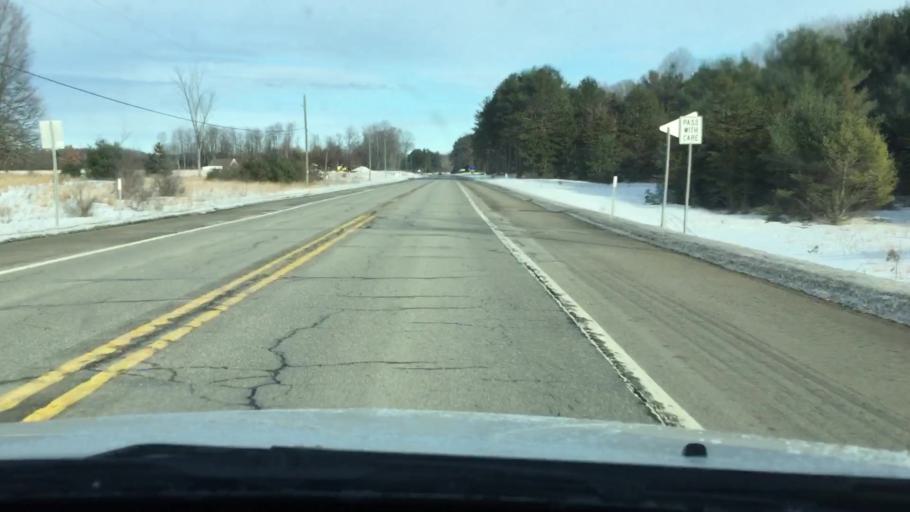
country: US
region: Michigan
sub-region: Wexford County
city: Manton
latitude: 44.5870
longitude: -85.3499
